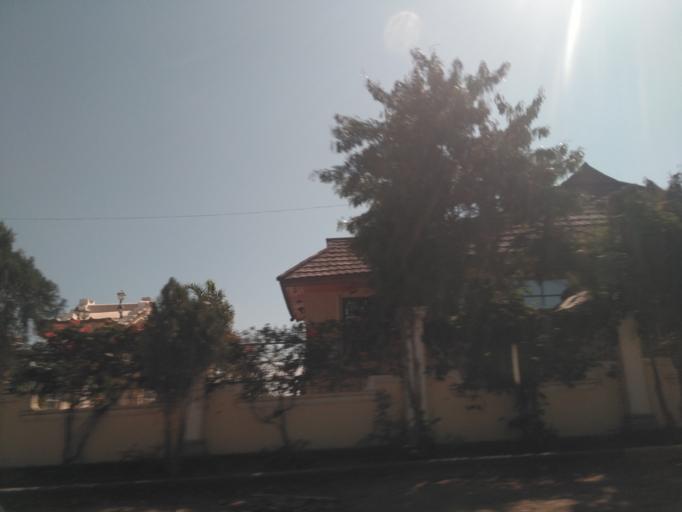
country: TZ
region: Dodoma
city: Dodoma
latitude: -6.1683
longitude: 35.7458
